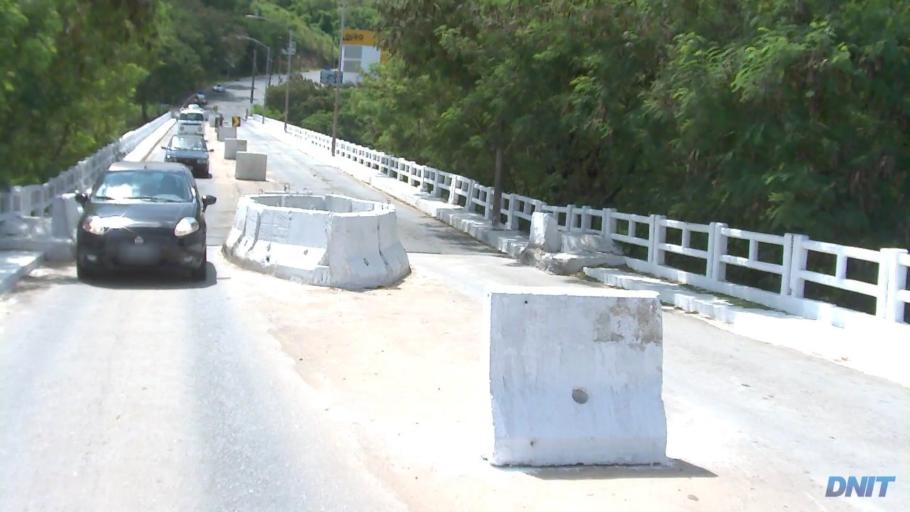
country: BR
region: Minas Gerais
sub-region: Coronel Fabriciano
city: Coronel Fabriciano
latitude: -19.5255
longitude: -42.6403
